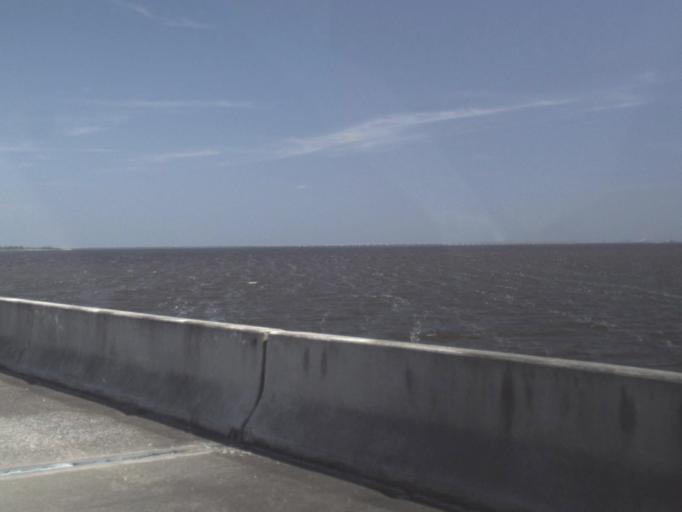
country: US
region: Florida
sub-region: Franklin County
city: Apalachicola
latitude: 29.7311
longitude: -84.9326
